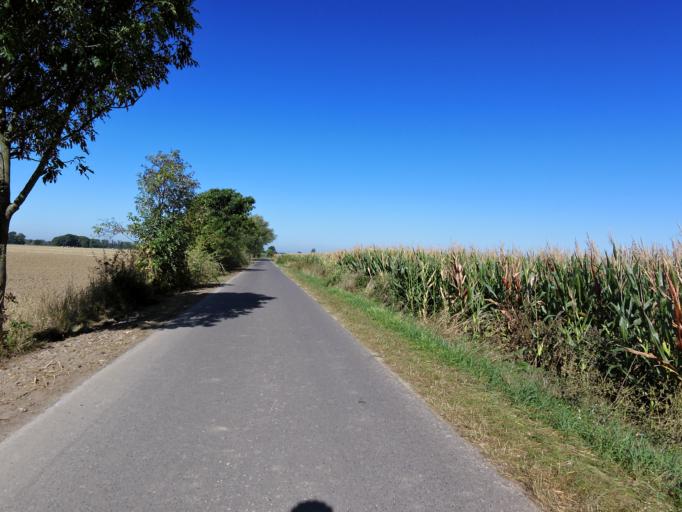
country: DE
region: Saxony
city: Elsnig
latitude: 51.6142
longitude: 12.9599
